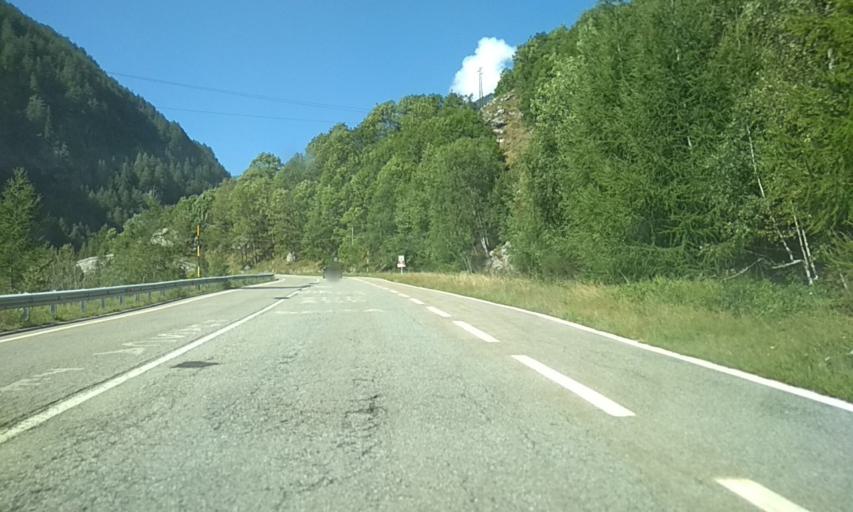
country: IT
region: Piedmont
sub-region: Provincia di Torino
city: Noasca
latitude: 45.4541
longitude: 7.3066
